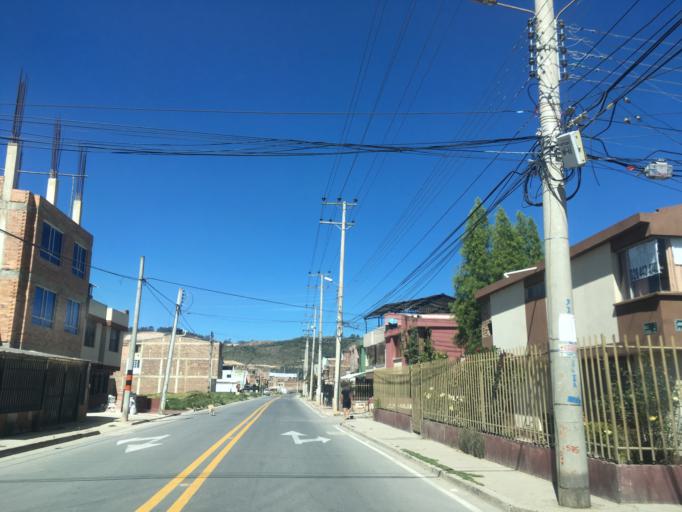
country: CO
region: Boyaca
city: Sogamoso
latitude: 5.7102
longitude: -72.9437
